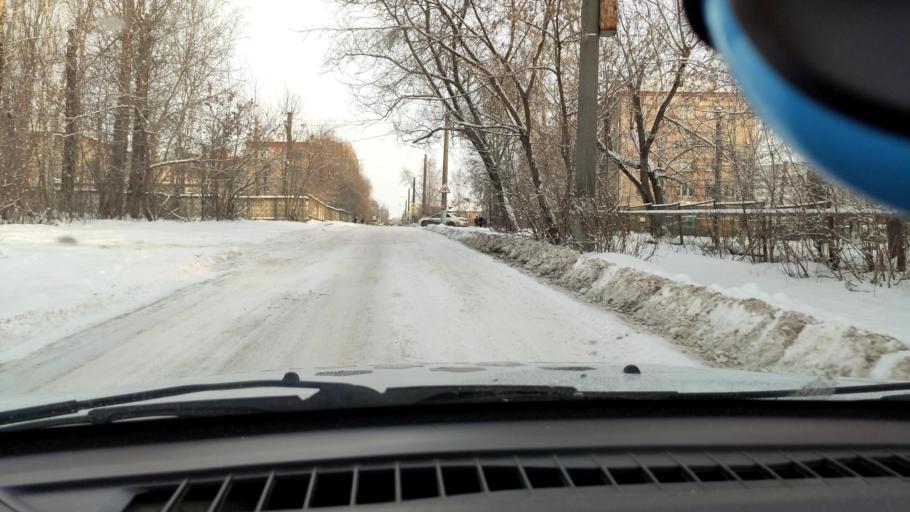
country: RU
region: Perm
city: Perm
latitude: 58.0981
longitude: 56.2913
